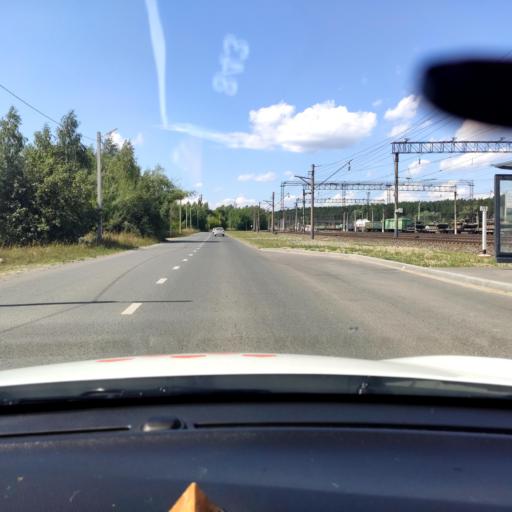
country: RU
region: Tatarstan
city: Osinovo
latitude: 55.8215
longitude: 48.8546
